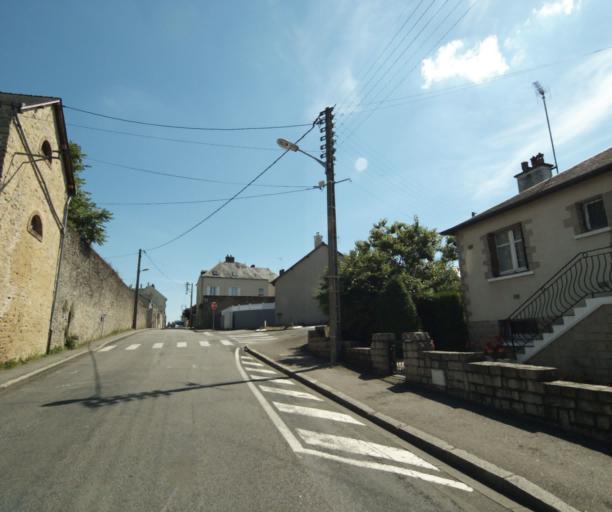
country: FR
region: Pays de la Loire
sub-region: Departement de la Mayenne
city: Laval
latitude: 48.0718
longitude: -0.7855
